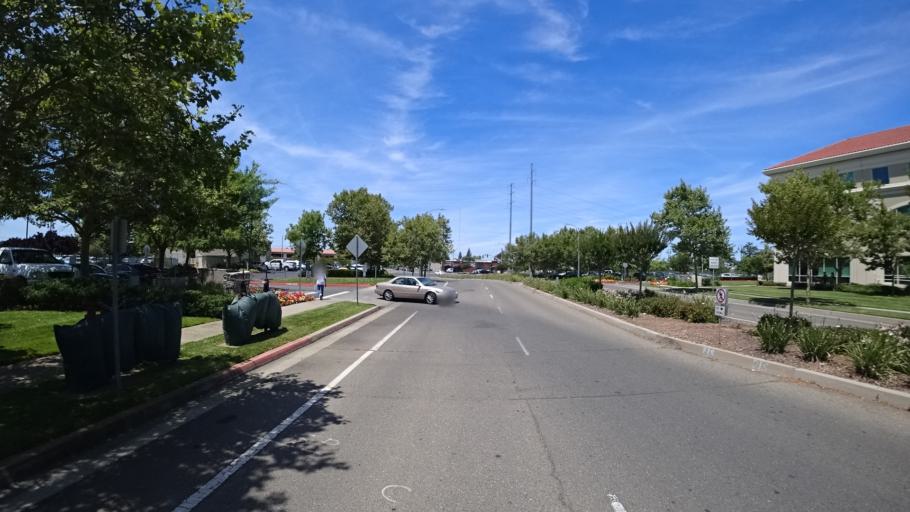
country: US
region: California
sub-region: Sacramento County
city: Rosemont
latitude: 38.5419
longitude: -121.4076
